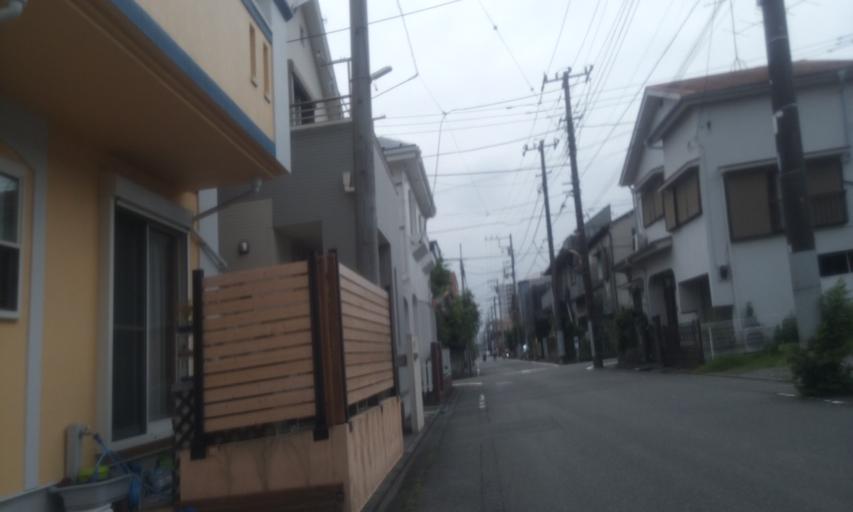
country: JP
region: Tokyo
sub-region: Machida-shi
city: Machida
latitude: 35.5755
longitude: 139.3812
